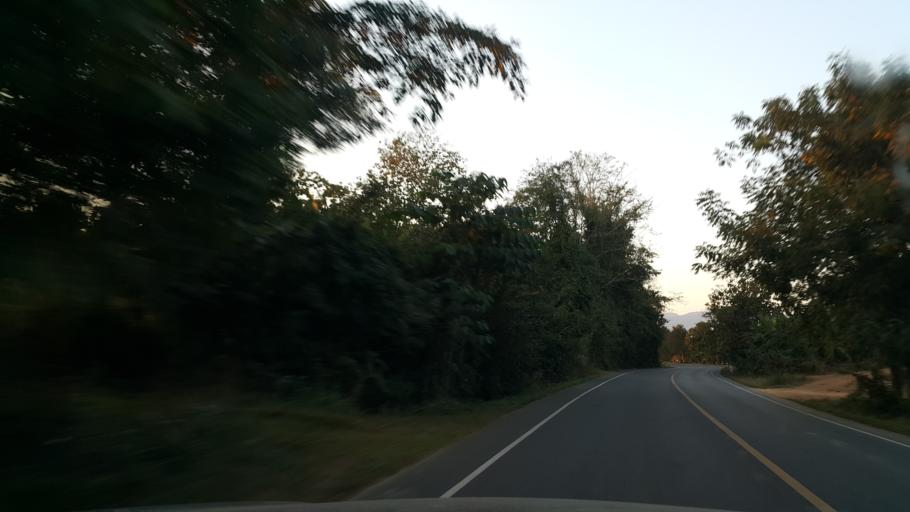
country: TH
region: Phrae
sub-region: Amphoe Wang Chin
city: Wang Chin
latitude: 17.8601
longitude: 99.6251
